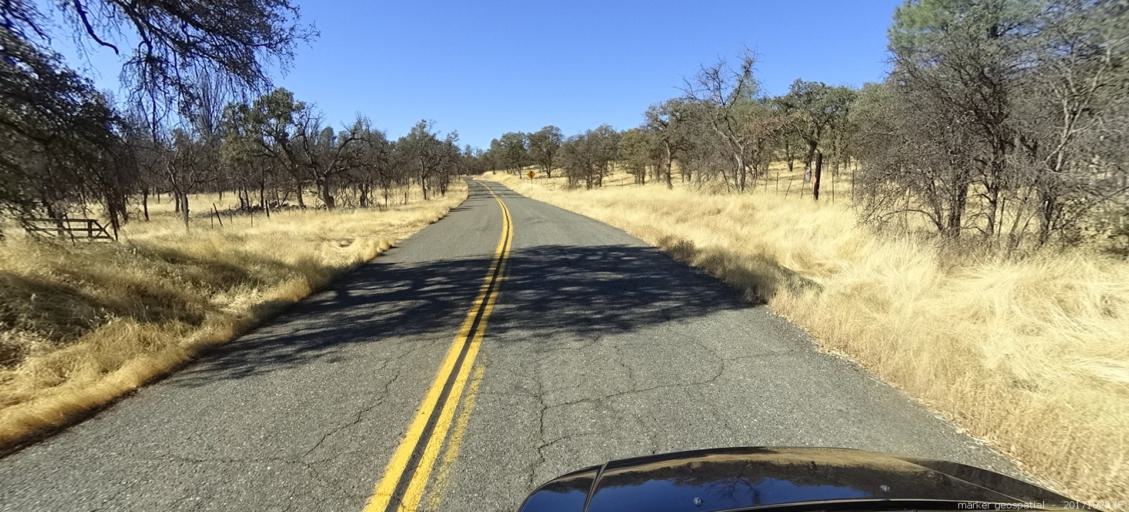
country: US
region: California
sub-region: Trinity County
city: Lewiston
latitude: 40.4249
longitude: -122.7580
